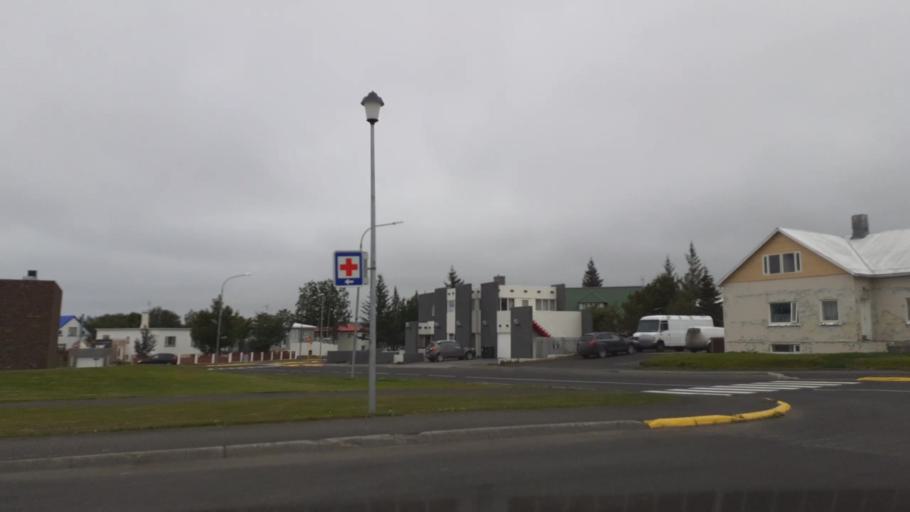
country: IS
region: Northeast
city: Dalvik
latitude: 65.9720
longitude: -18.5337
